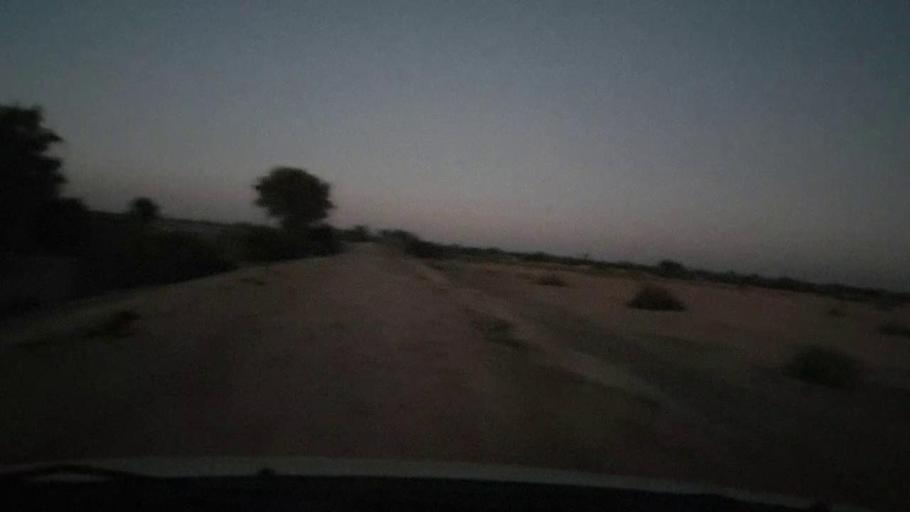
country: PK
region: Sindh
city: Phulji
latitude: 26.9029
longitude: 67.4769
